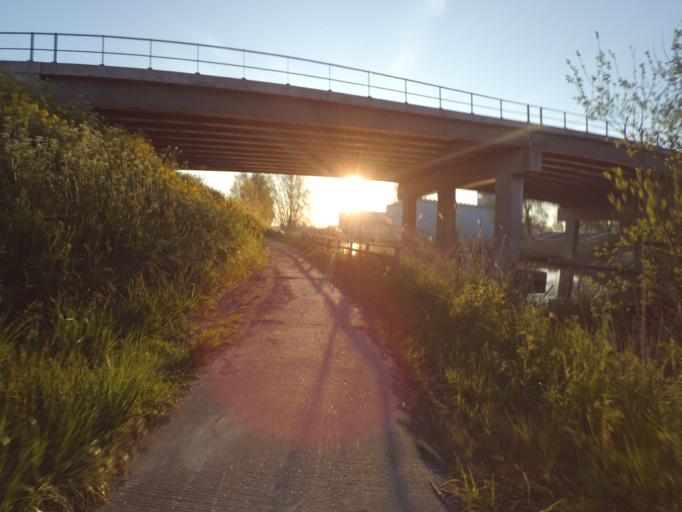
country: NL
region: Flevoland
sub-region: Gemeente Zeewolde
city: Zeewolde
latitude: 52.3561
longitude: 5.4886
